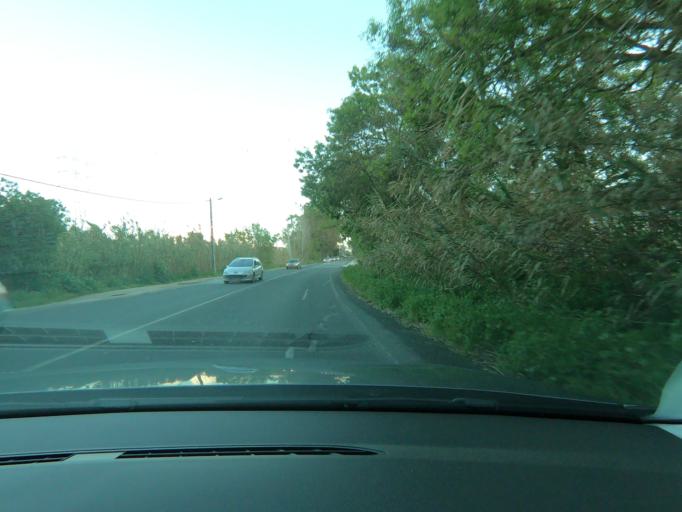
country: PT
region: Lisbon
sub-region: Alenquer
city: Carregado
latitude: 39.0177
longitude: -8.9732
